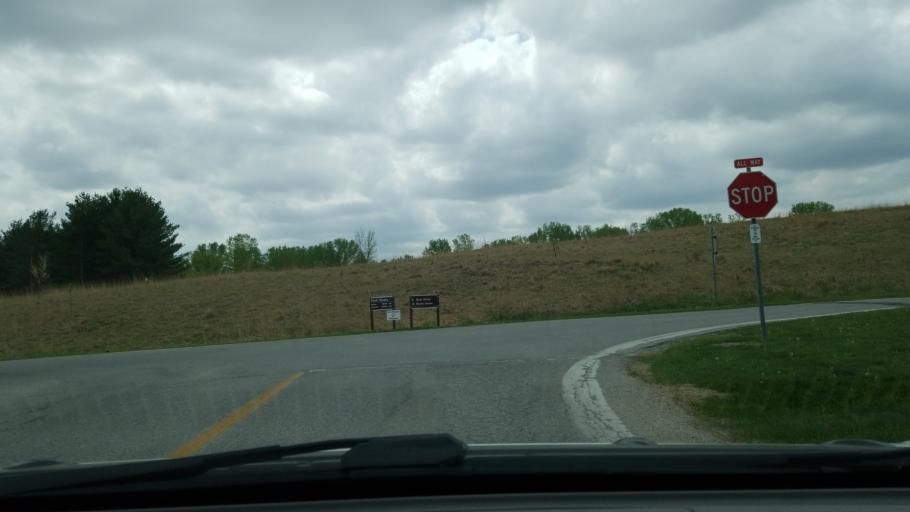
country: US
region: Nebraska
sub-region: Sarpy County
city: Chalco
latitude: 41.1702
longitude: -96.1607
